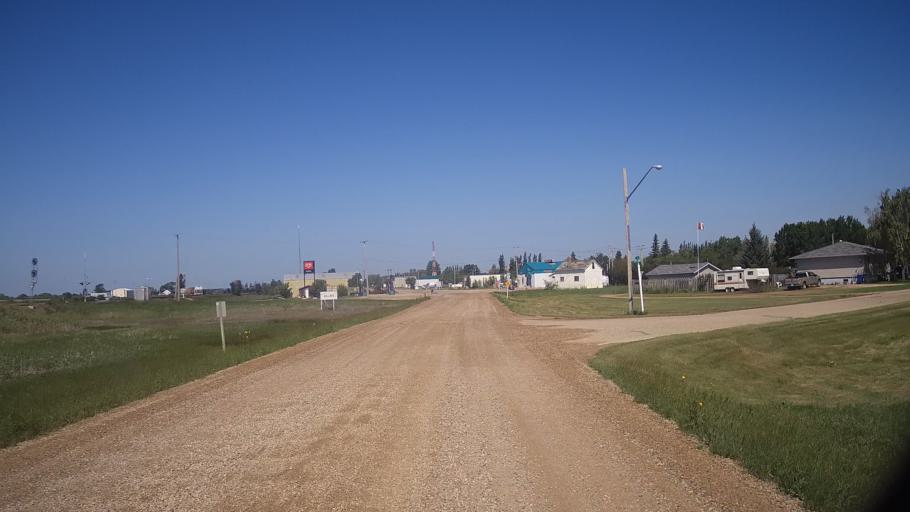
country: CA
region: Saskatchewan
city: Watrous
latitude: 51.8905
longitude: -106.0496
